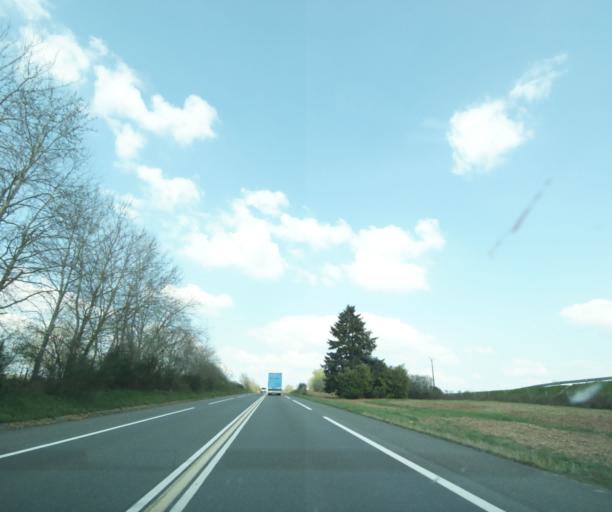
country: FR
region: Auvergne
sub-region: Departement de l'Allier
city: Montmarault
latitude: 46.3436
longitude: 2.9882
